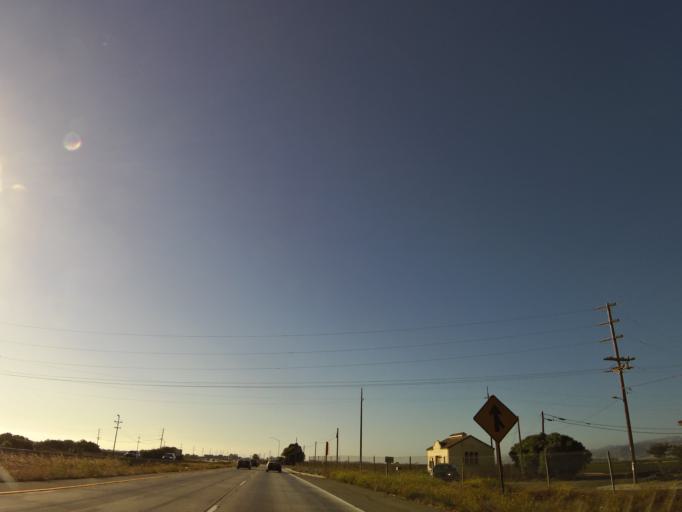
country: US
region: California
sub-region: Monterey County
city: Chualar
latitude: 36.5715
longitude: -121.5201
